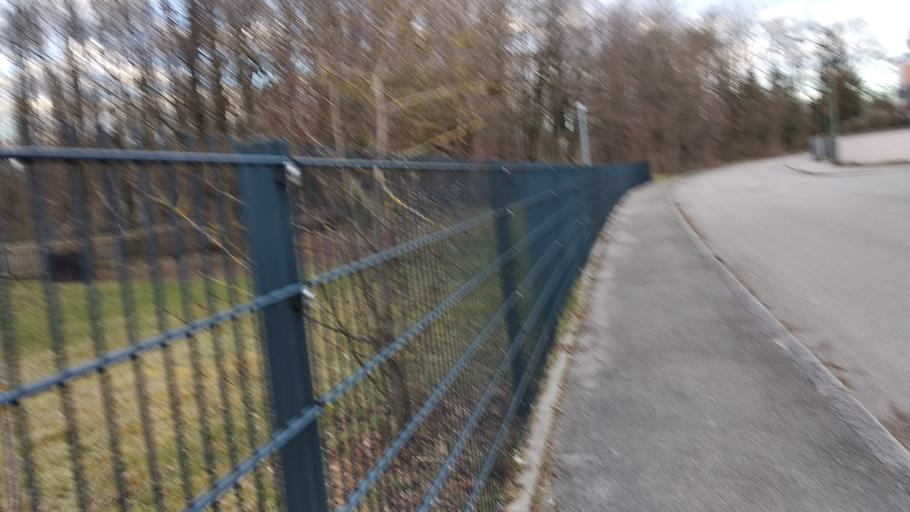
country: DE
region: Bavaria
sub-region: Upper Bavaria
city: Neubiberg
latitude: 48.0812
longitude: 11.6832
